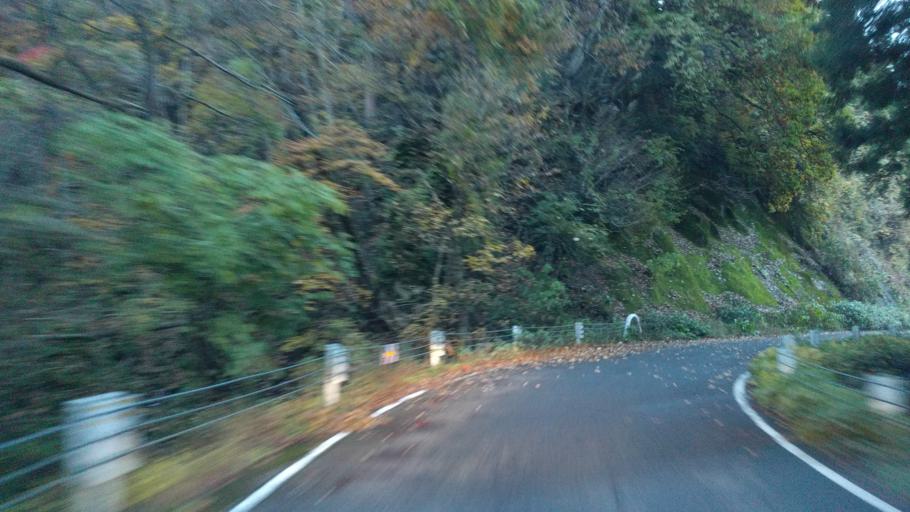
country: JP
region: Fukushima
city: Kitakata
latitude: 37.5103
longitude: 139.6986
